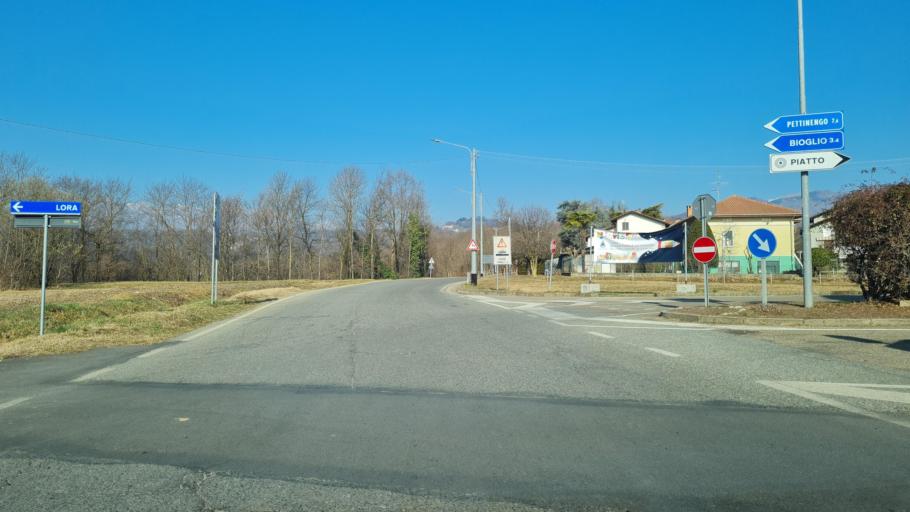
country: IT
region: Piedmont
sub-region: Provincia di Biella
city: Piatto
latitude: 45.5882
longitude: 8.1353
